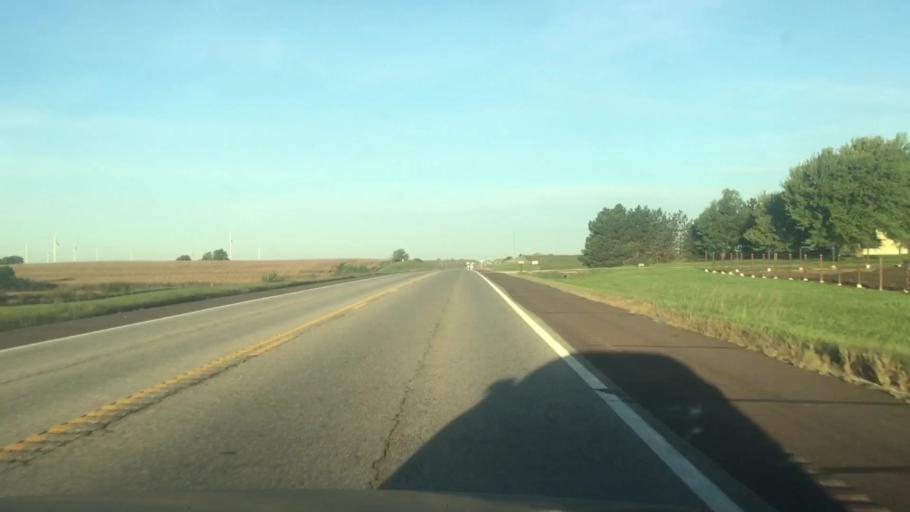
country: US
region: Kansas
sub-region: Nemaha County
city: Seneca
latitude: 39.8425
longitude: -96.3182
